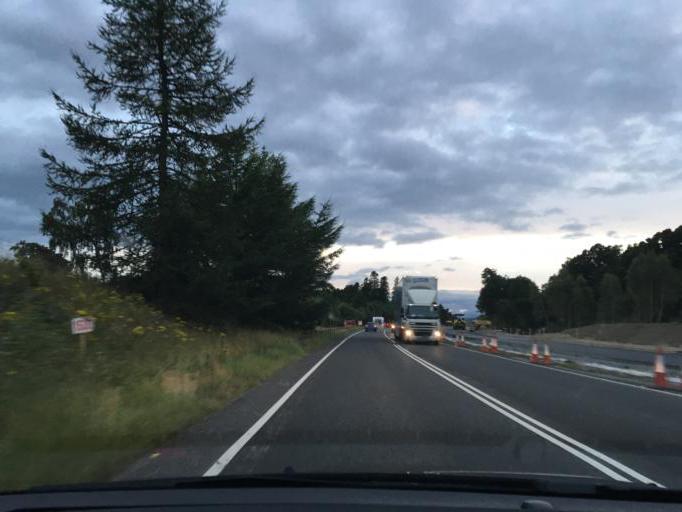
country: GB
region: Scotland
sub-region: Highland
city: Kingussie
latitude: 57.1185
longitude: -3.9458
